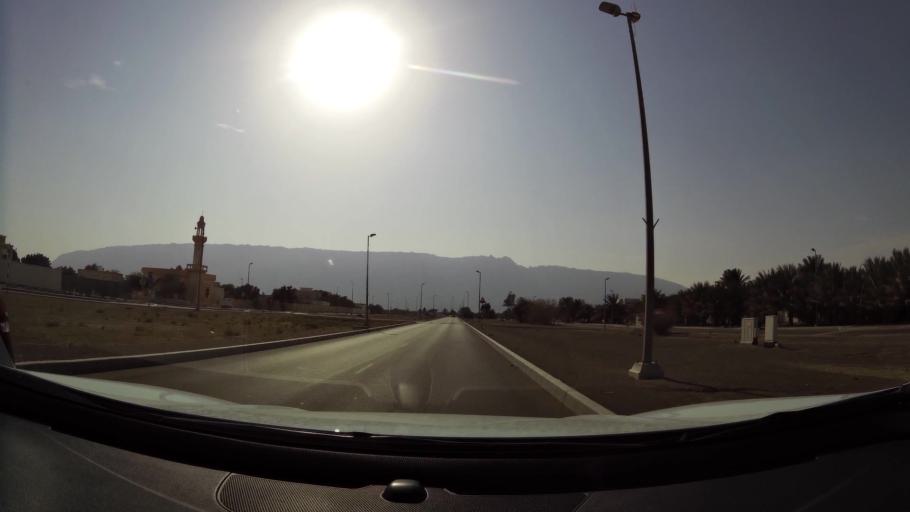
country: AE
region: Abu Dhabi
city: Al Ain
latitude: 24.0652
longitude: 55.8422
